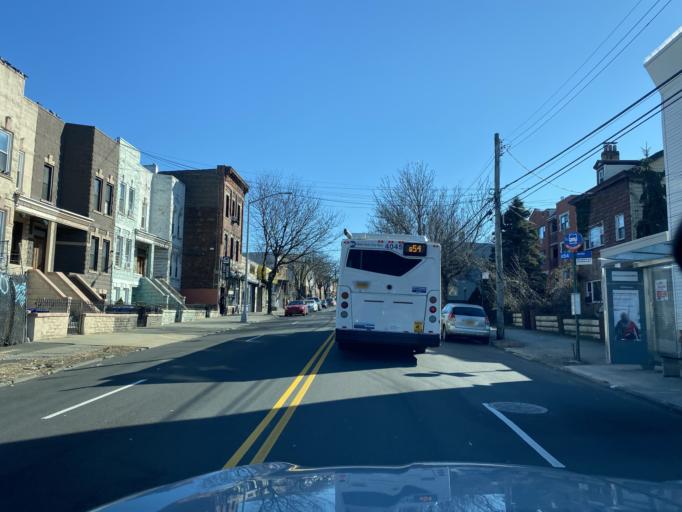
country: US
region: New York
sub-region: Queens County
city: Long Island City
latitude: 40.7133
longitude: -73.9128
